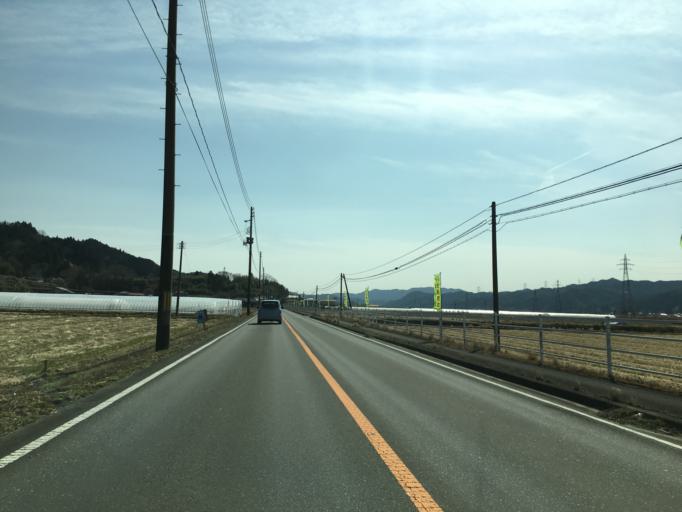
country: JP
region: Ibaraki
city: Daigo
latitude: 36.9210
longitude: 140.4159
